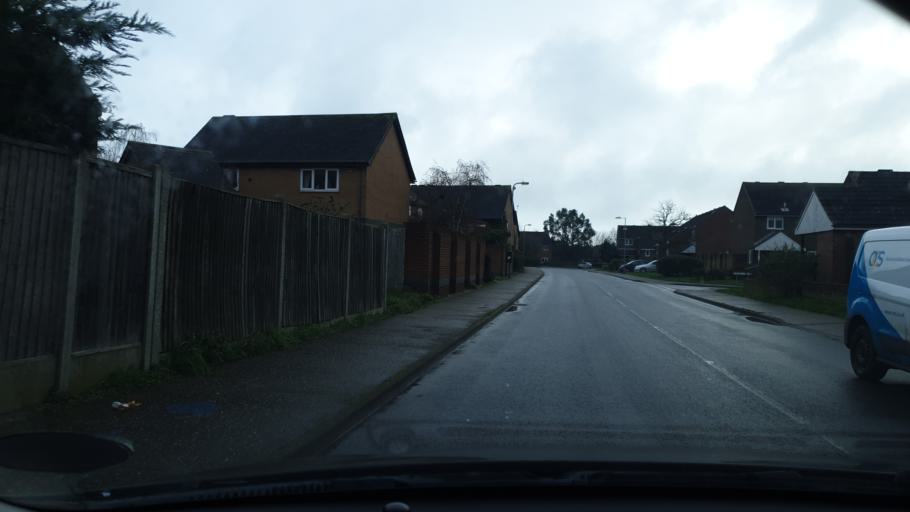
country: GB
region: England
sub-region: Essex
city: Clacton-on-Sea
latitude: 51.7981
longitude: 1.1252
